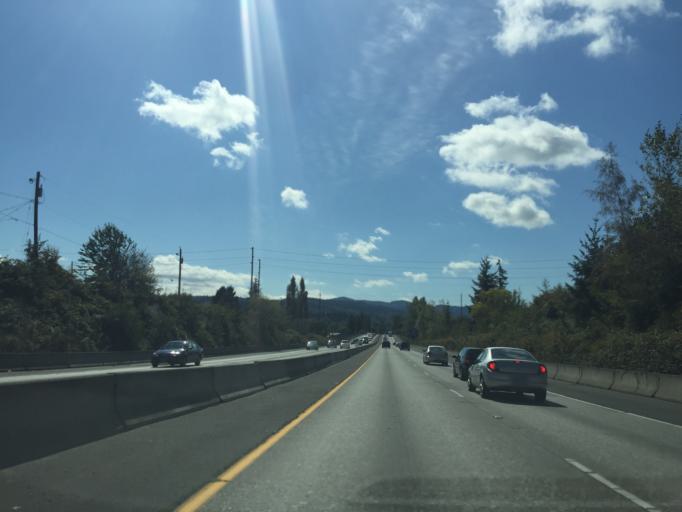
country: US
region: Washington
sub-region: Whatcom County
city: Bellingham
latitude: 48.7629
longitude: -122.4618
